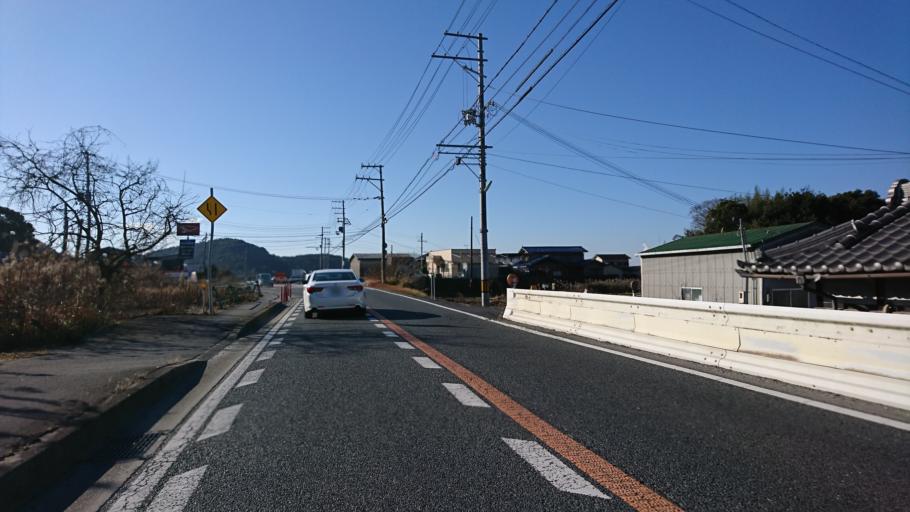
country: JP
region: Hyogo
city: Kakogawacho-honmachi
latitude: 34.8095
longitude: 134.8359
